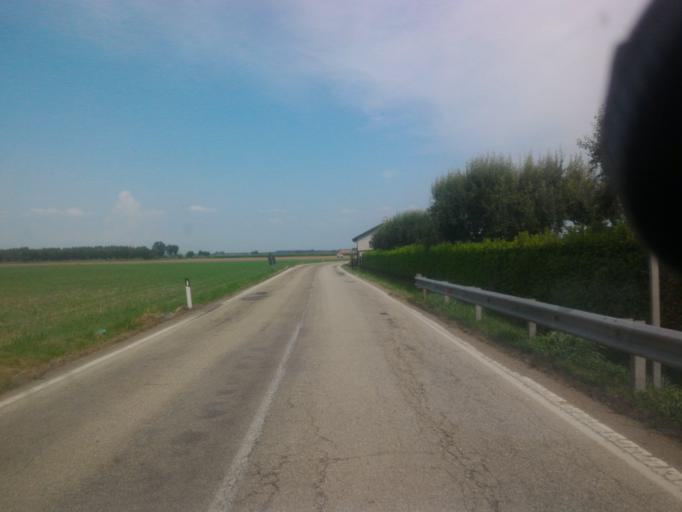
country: IT
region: Piedmont
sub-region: Provincia di Torino
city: Buriasco
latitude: 44.8544
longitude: 7.4484
